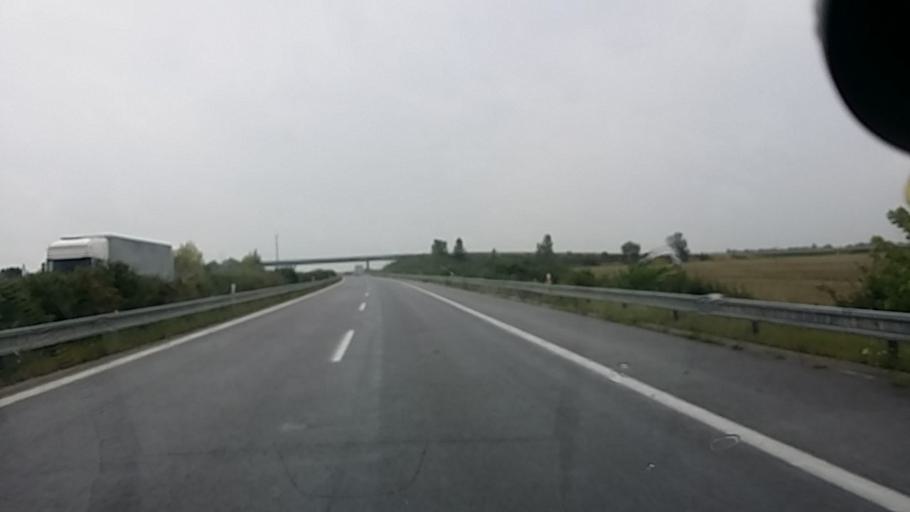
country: AT
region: Burgenland
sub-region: Politischer Bezirk Neusiedl am See
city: Deutsch Jahrndorf
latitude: 48.0434
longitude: 17.1147
